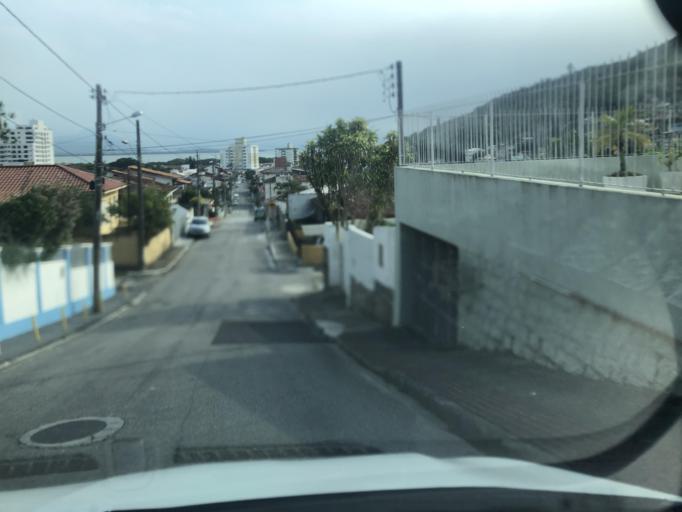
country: BR
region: Santa Catarina
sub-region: Florianopolis
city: Saco dos Limoes
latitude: -27.6038
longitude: -48.5349
